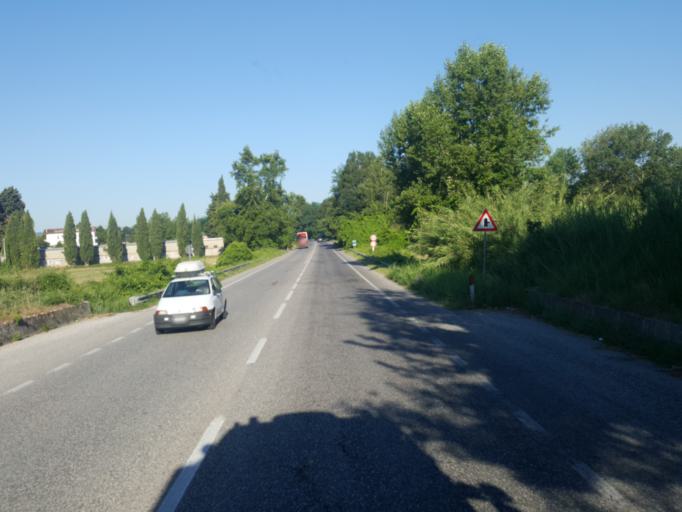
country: IT
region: The Marches
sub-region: Provincia di Pesaro e Urbino
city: Montelabbate
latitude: 43.8519
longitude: 12.7943
